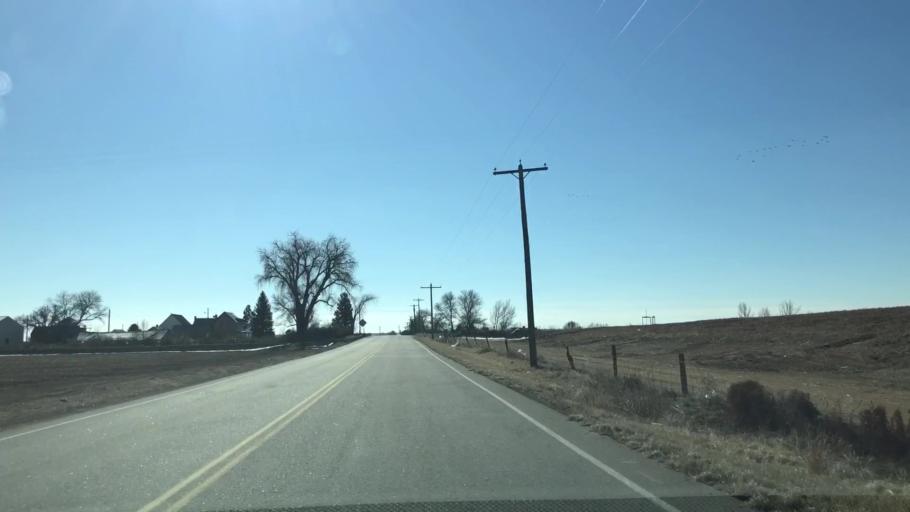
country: US
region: Colorado
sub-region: Weld County
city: Windsor
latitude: 40.5116
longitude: -104.9442
